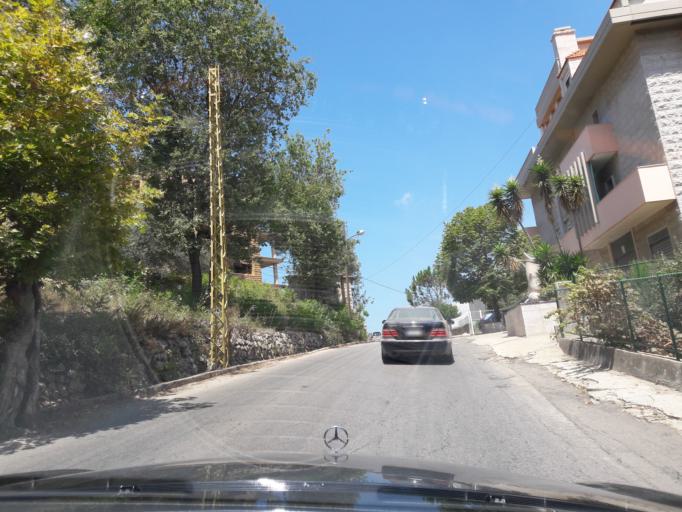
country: LB
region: Mont-Liban
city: Djounie
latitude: 33.9260
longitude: 35.6630
